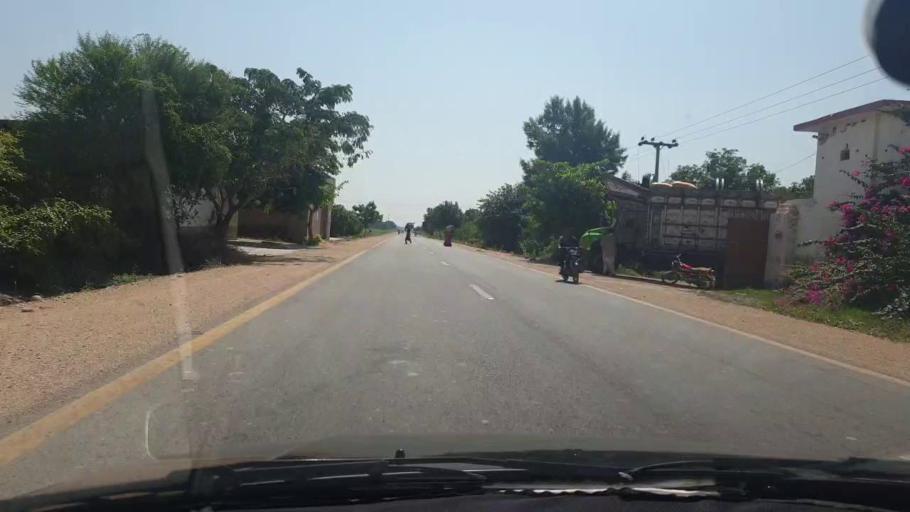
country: PK
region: Sindh
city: Chambar
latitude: 25.3215
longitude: 68.8020
